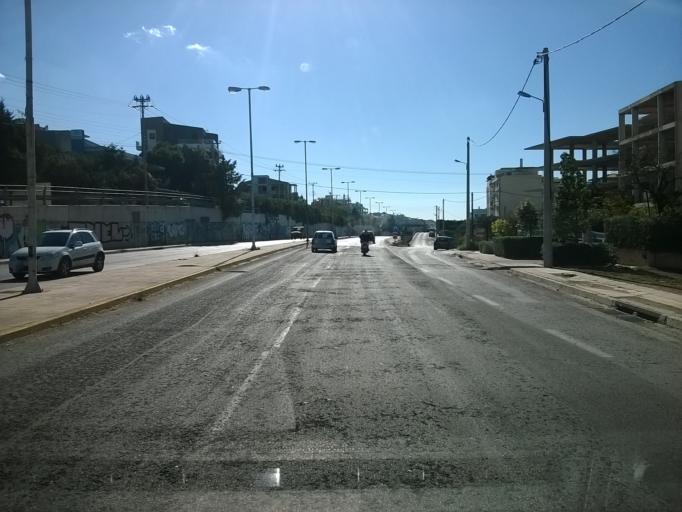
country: GR
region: Attica
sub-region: Nomarchia Anatolikis Attikis
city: Voula
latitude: 37.8412
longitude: 23.7719
